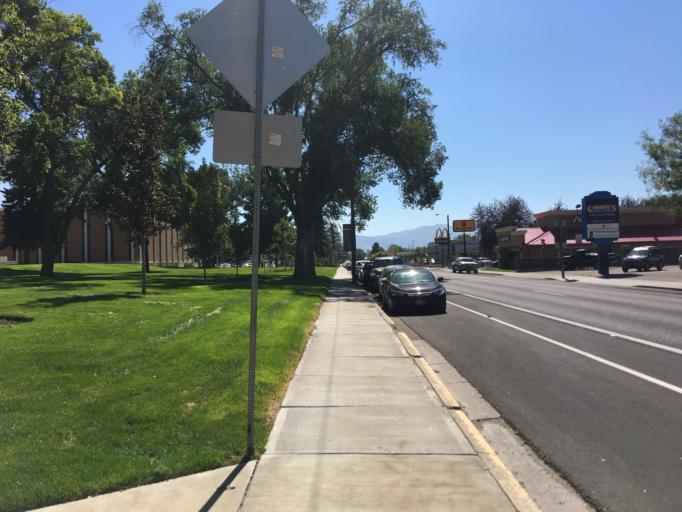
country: US
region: Idaho
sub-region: Bannock County
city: Pocatello
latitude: 42.8606
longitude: -112.4364
